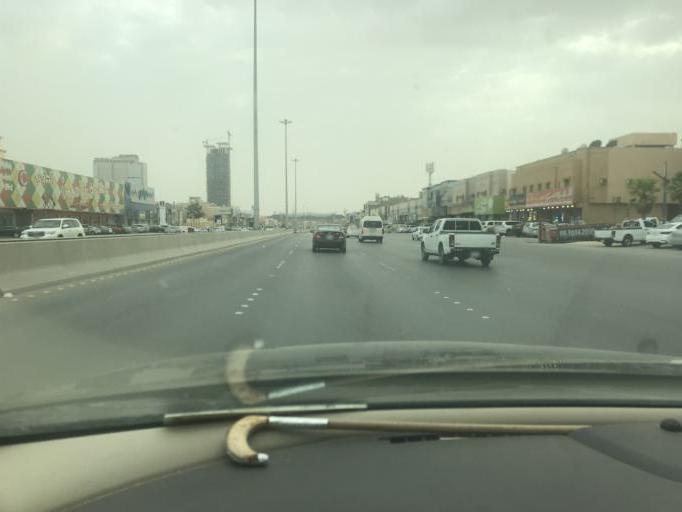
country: SA
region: Ar Riyad
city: Riyadh
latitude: 24.8149
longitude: 46.6334
